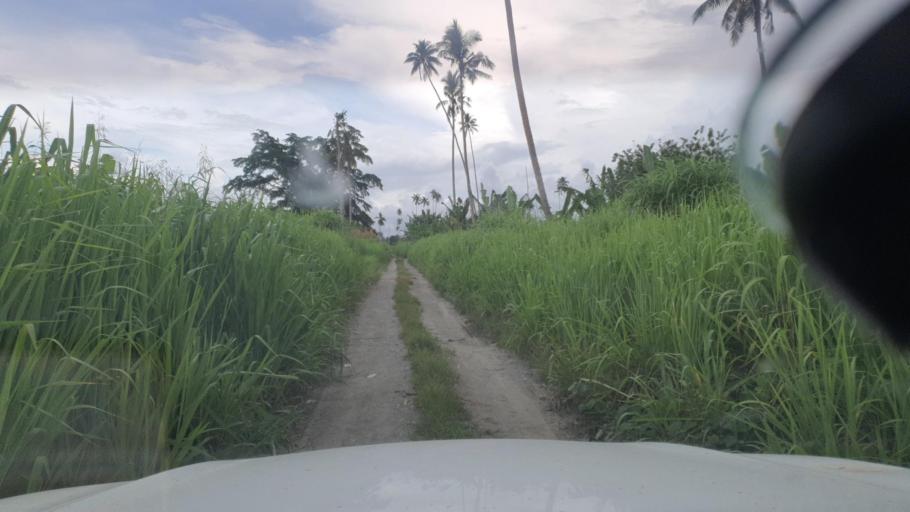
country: SB
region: Guadalcanal
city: Honiara
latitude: -9.4369
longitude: 160.2815
